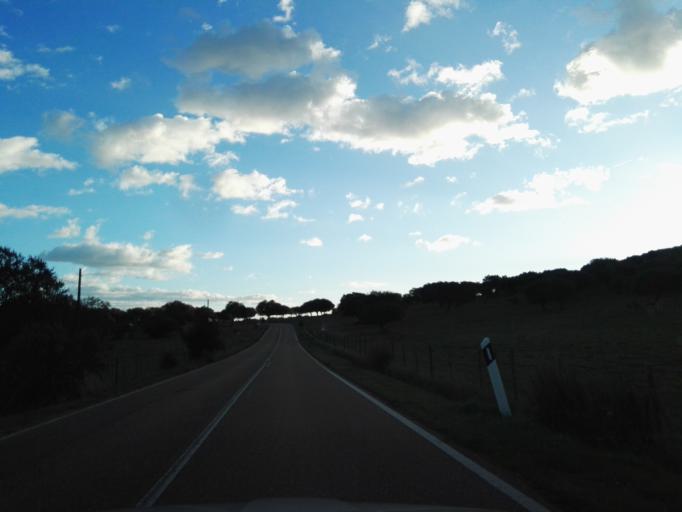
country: PT
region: Portalegre
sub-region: Elvas
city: Elvas
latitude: 38.8214
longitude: -7.1664
